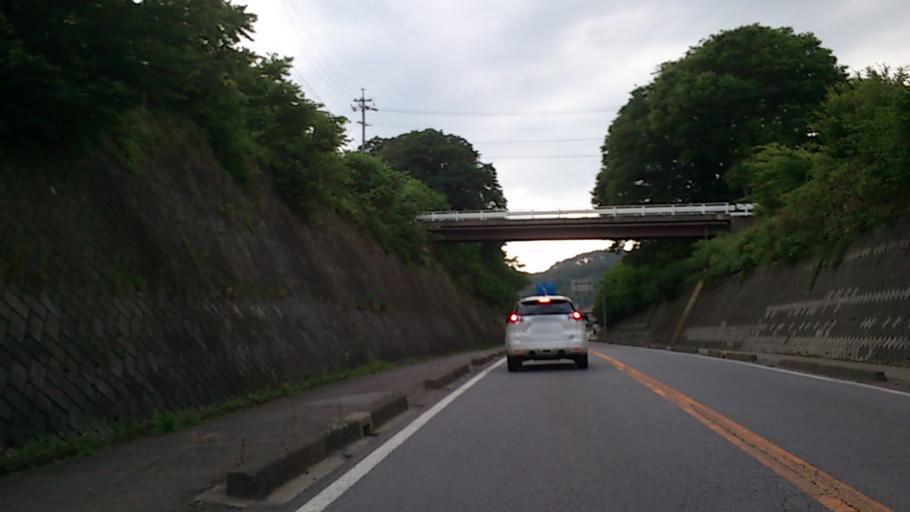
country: JP
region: Nagano
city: Komoro
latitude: 36.2698
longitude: 138.3902
